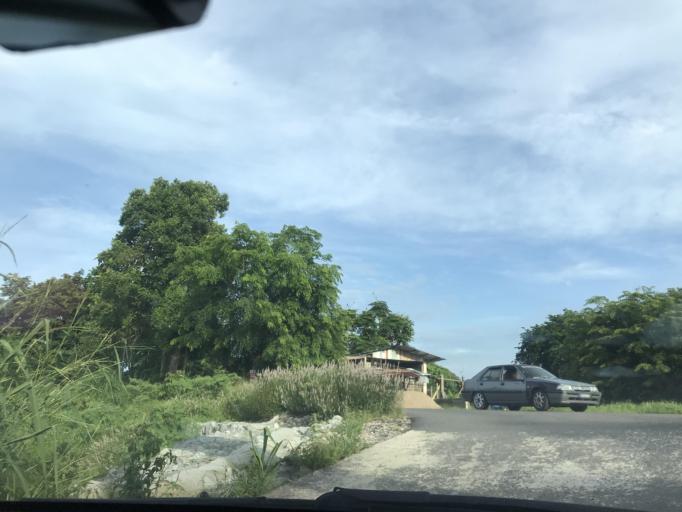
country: MY
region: Kelantan
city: Kota Bharu
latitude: 6.1383
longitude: 102.2242
